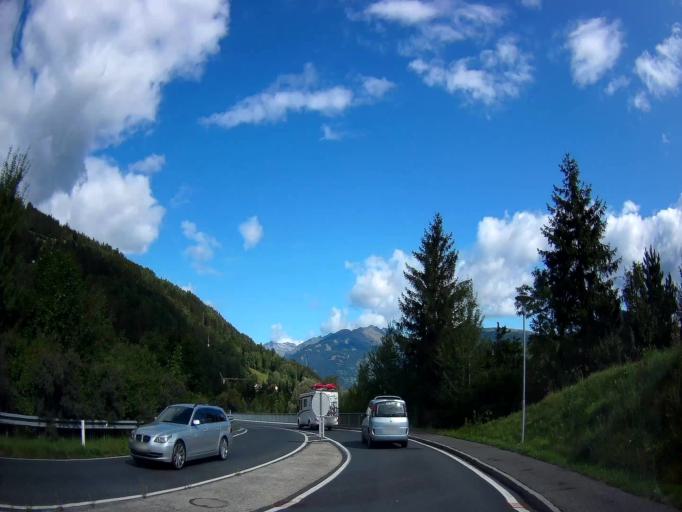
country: AT
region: Carinthia
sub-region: Politischer Bezirk Spittal an der Drau
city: Gmuend
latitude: 46.9020
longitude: 13.5333
